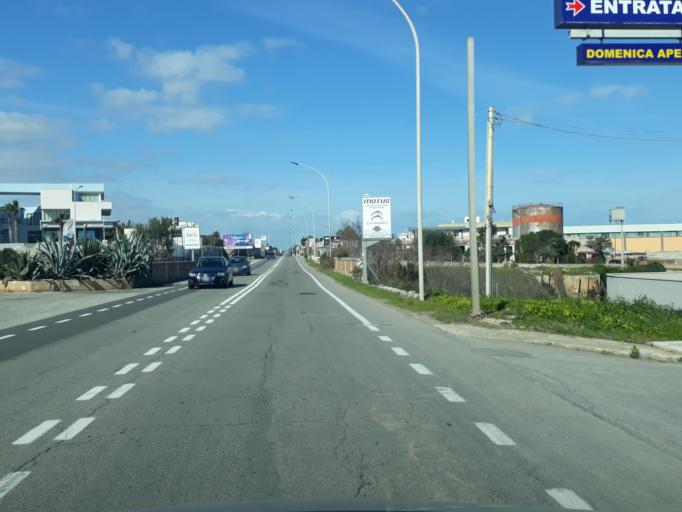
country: IT
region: Apulia
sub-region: Provincia di Bari
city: Monopoli
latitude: 40.9690
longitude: 17.2679
